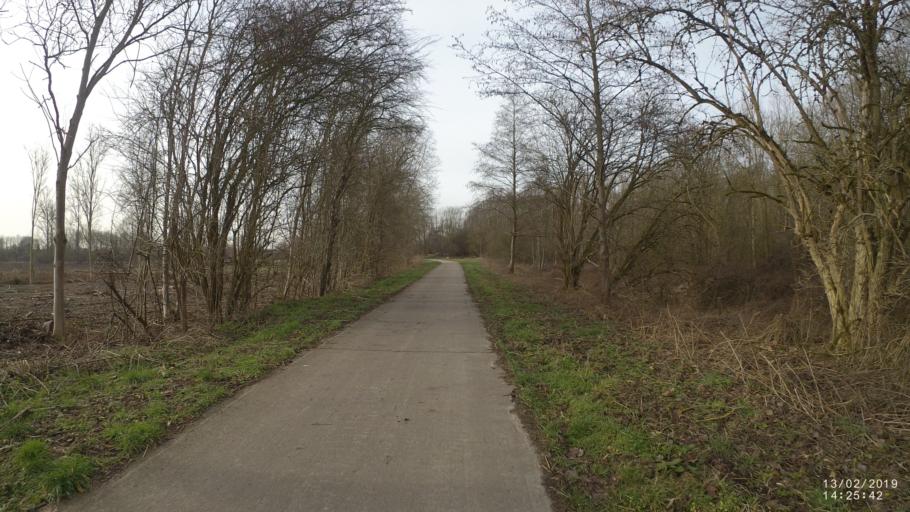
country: BE
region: Flanders
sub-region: Provincie Vlaams-Brabant
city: Zoutleeuw
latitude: 50.8442
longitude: 5.0650
